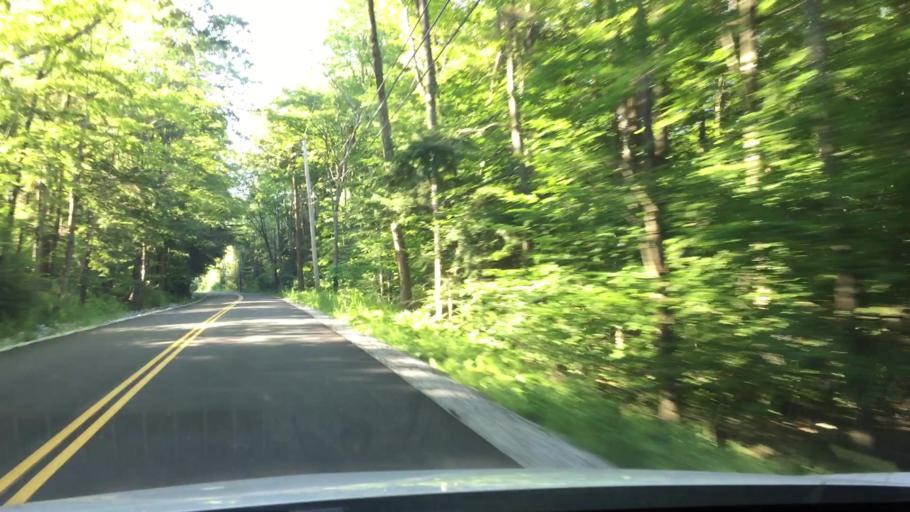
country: US
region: Massachusetts
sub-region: Berkshire County
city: Lee
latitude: 42.2847
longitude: -73.2134
